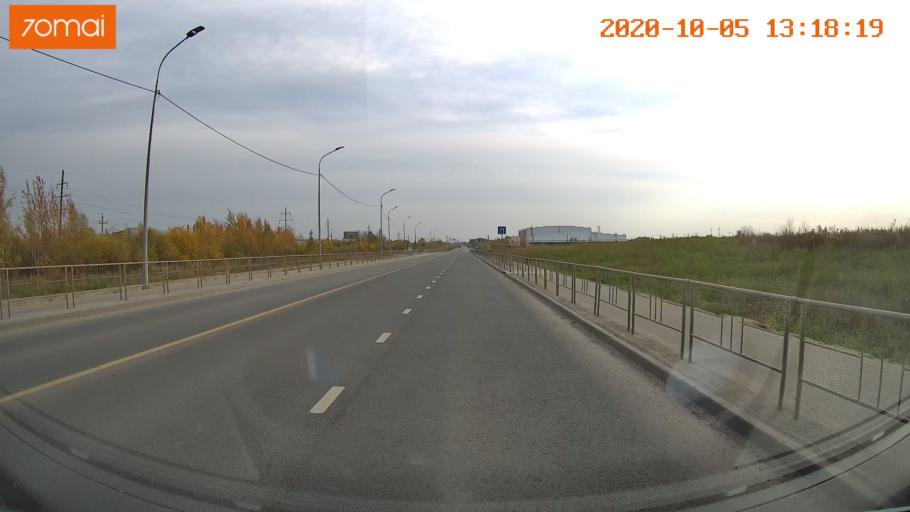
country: RU
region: Ivanovo
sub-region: Gorod Ivanovo
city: Ivanovo
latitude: 56.9783
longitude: 40.9189
